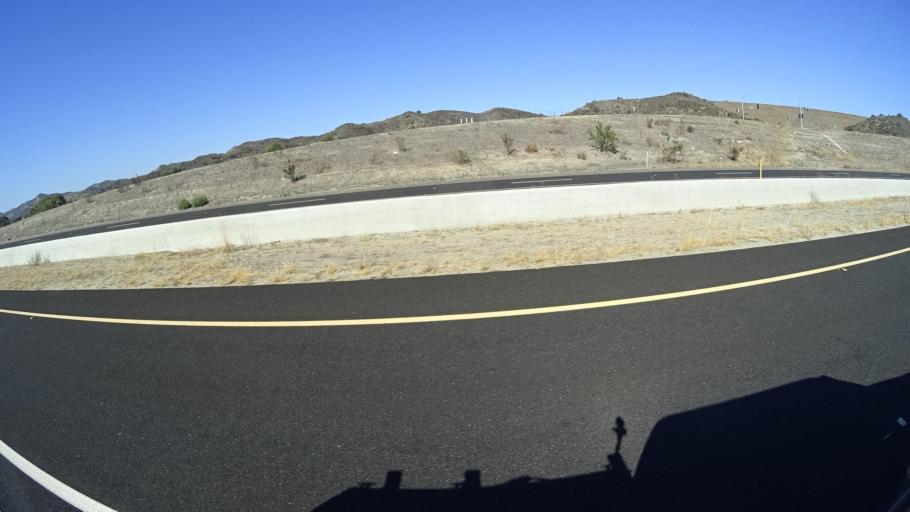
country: US
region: California
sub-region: Orange County
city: Las Flores
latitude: 33.5867
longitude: -117.6071
